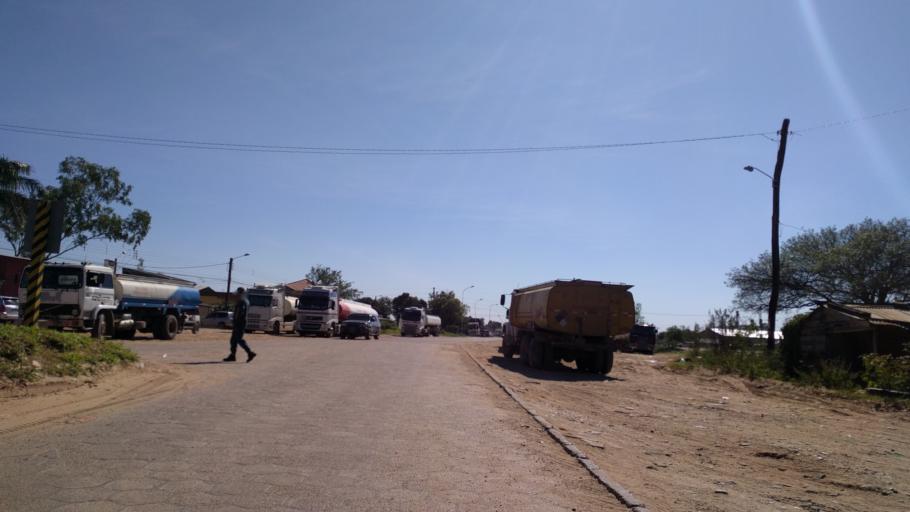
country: BO
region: Santa Cruz
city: Santa Cruz de la Sierra
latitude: -17.8749
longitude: -63.1935
